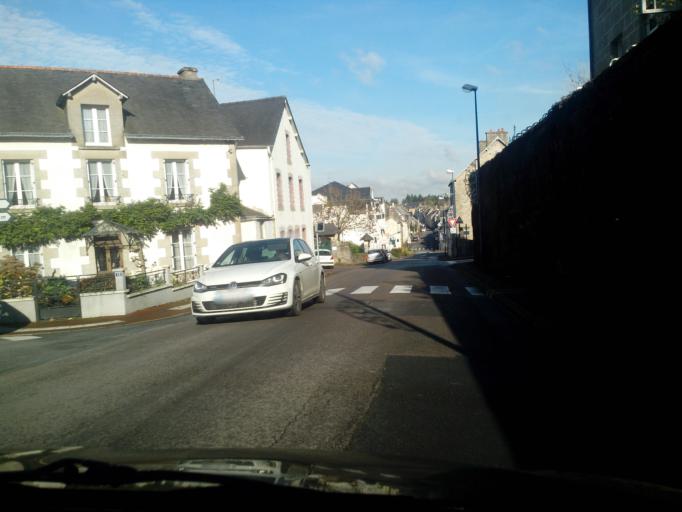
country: FR
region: Brittany
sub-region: Departement du Morbihan
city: Ploermel
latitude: 47.9337
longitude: -2.3992
